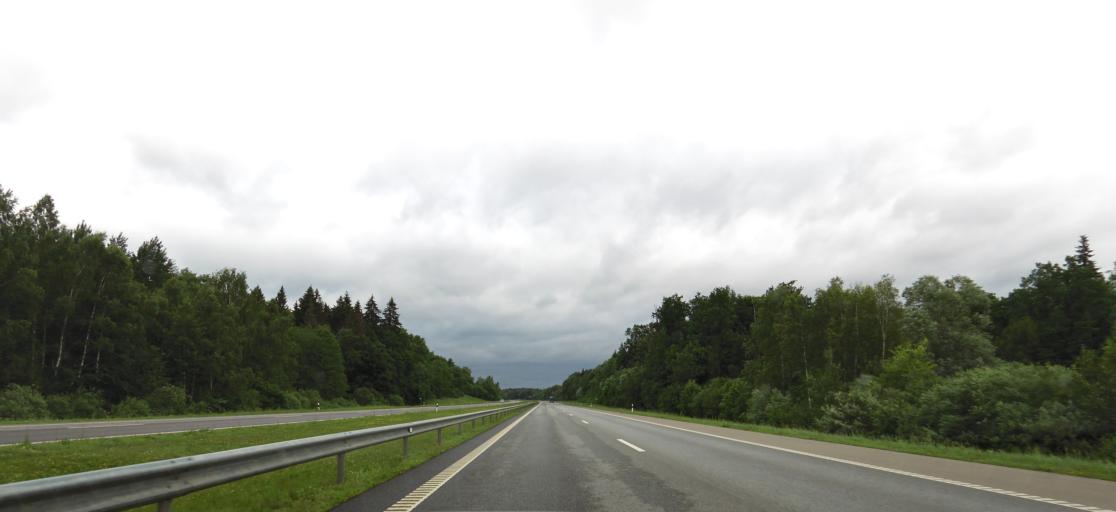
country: LT
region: Vilnius County
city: Pasilaiciai
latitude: 54.8379
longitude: 25.1174
